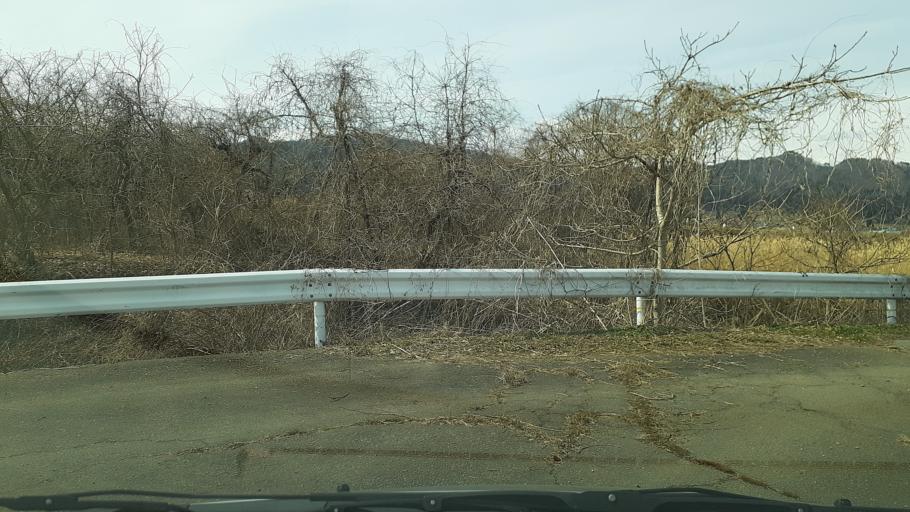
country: JP
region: Fukushima
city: Kitakata
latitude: 37.4567
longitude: 139.8240
